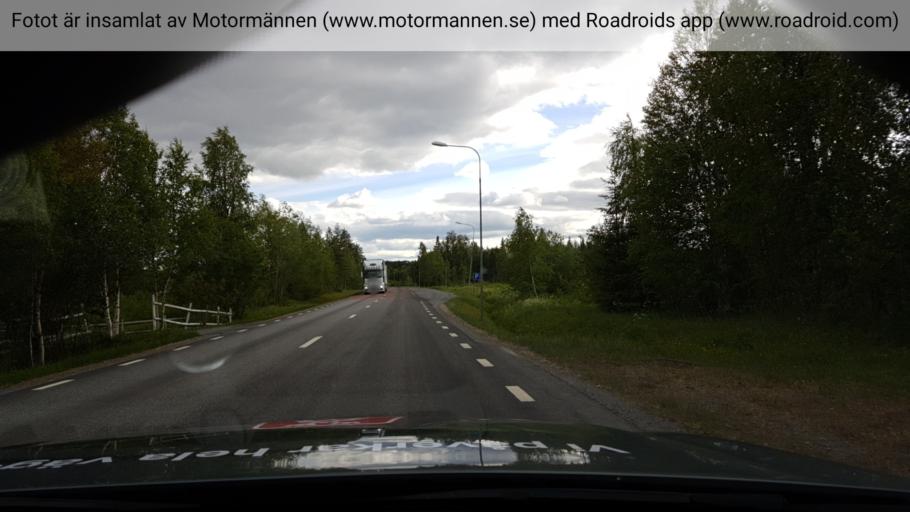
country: SE
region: Jaemtland
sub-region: Stroemsunds Kommun
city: Stroemsund
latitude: 63.8363
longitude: 15.5197
